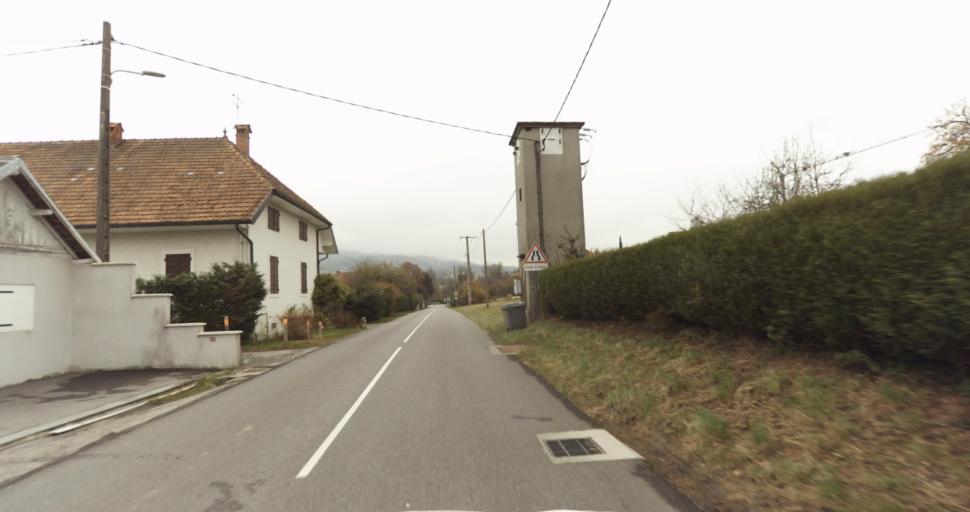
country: FR
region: Rhone-Alpes
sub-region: Departement de la Haute-Savoie
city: Cusy
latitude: 45.7722
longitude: 6.0240
